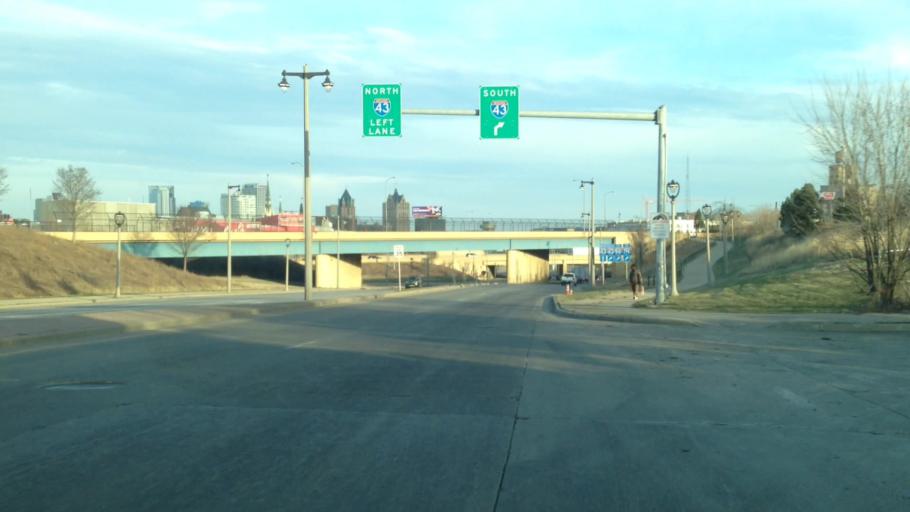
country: US
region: Wisconsin
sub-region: Milwaukee County
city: Milwaukee
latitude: 43.0523
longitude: -87.9285
